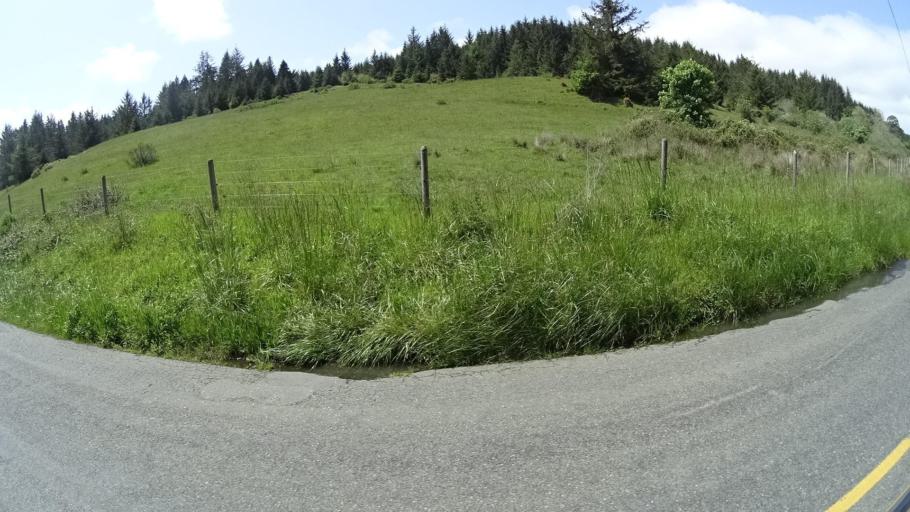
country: US
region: California
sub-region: Humboldt County
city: Humboldt Hill
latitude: 40.6700
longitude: -124.2090
